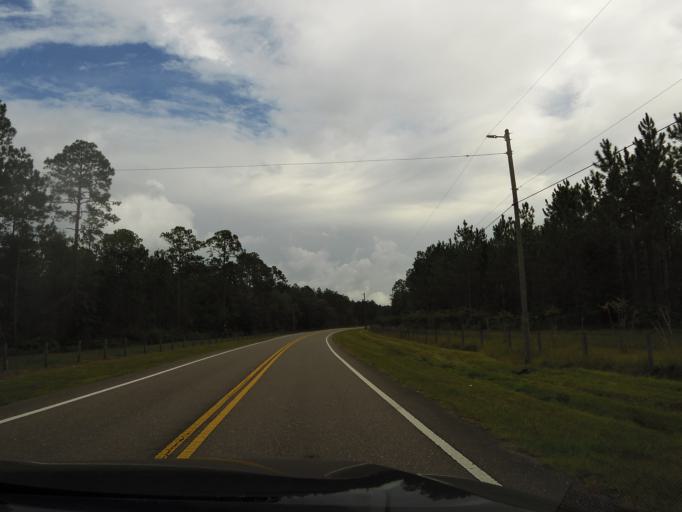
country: US
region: Florida
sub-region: Duval County
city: Baldwin
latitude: 30.3606
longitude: -81.9175
